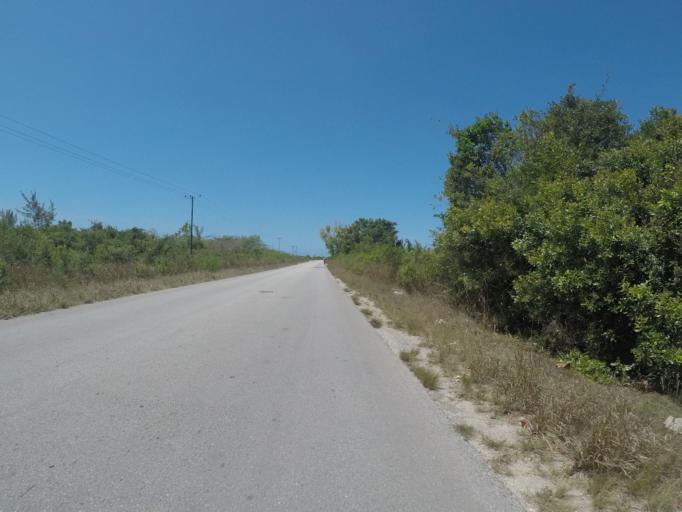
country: TZ
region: Zanzibar Central/South
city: Nganane
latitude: -6.2739
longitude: 39.4907
